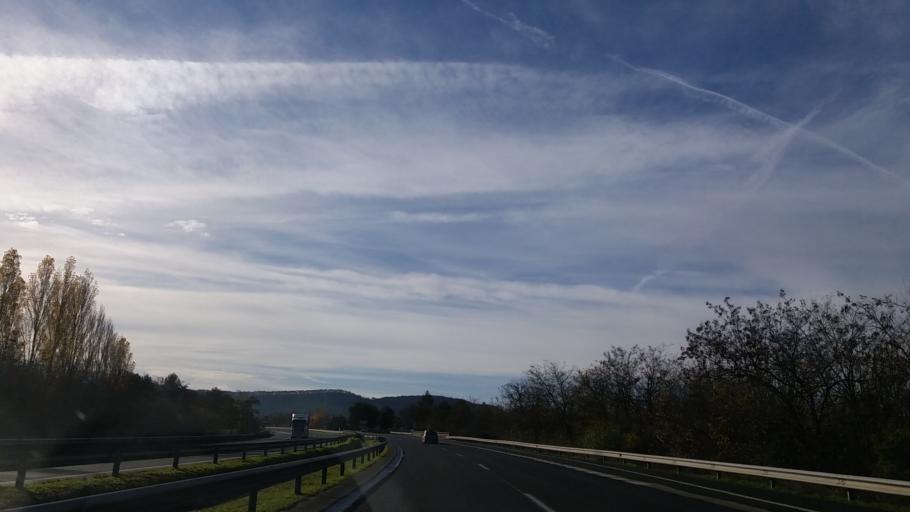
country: ES
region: Navarre
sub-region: Provincia de Navarra
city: Orkoien
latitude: 42.8200
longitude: -1.7149
